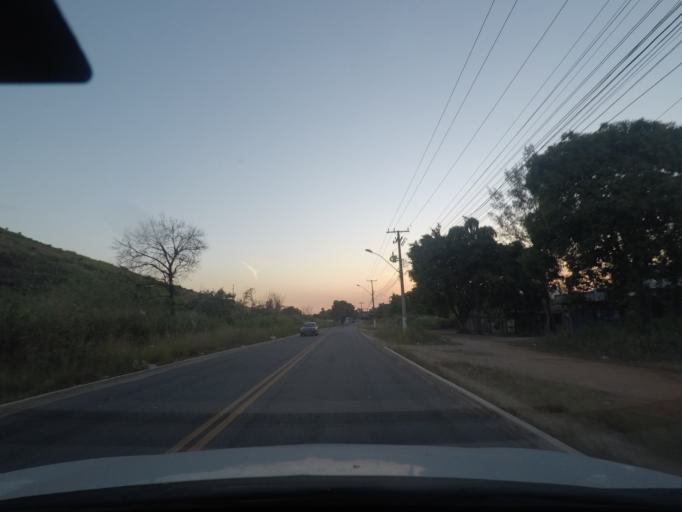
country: BR
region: Rio de Janeiro
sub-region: Niteroi
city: Niteroi
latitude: -22.9552
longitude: -42.9769
